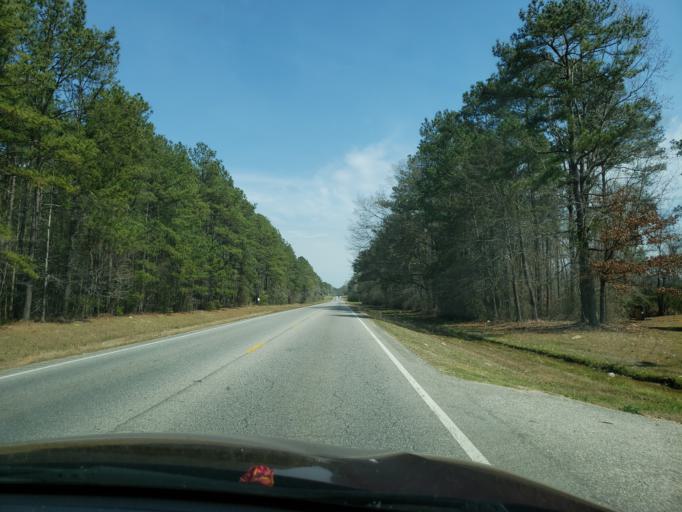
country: US
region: Alabama
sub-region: Elmore County
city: Elmore
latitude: 32.5444
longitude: -86.3038
